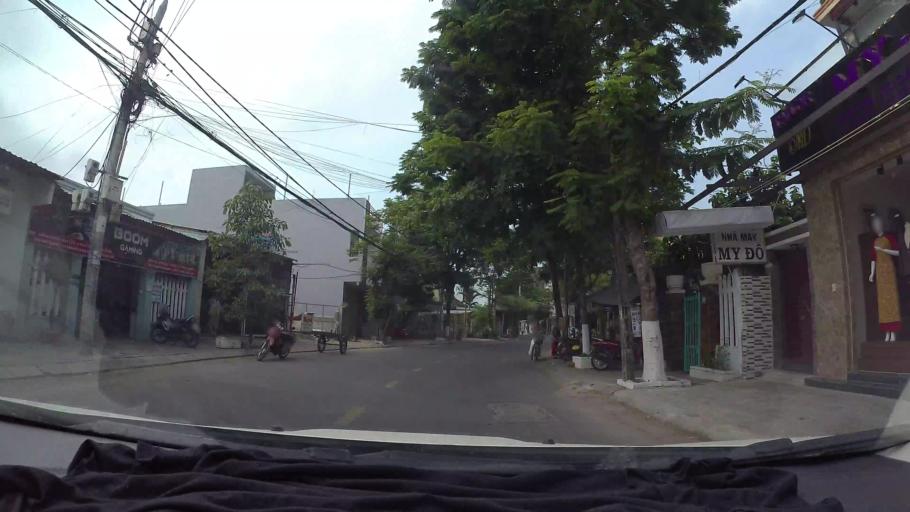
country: VN
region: Da Nang
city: Thanh Khe
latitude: 16.0533
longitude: 108.1793
